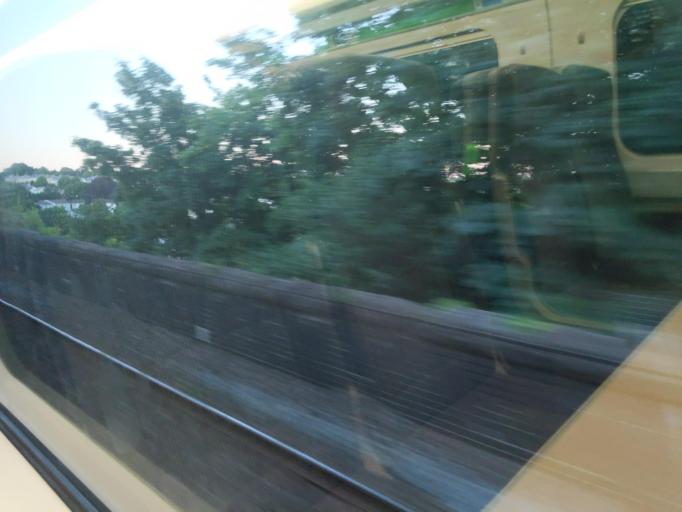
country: GB
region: England
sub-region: Cornwall
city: Truro
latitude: 50.2665
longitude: -5.0558
